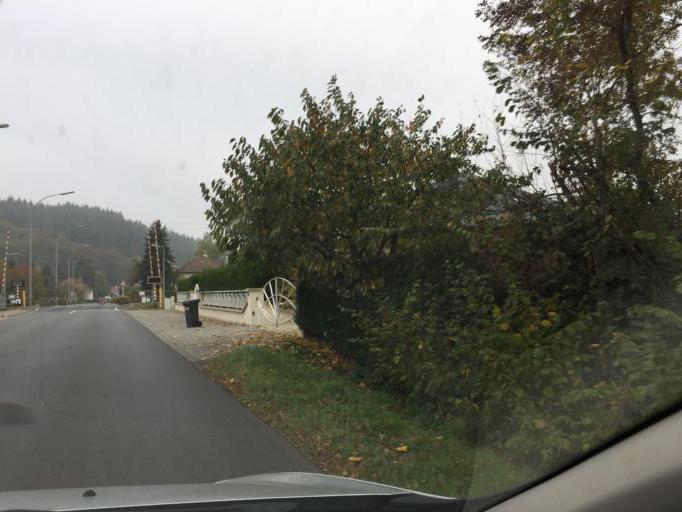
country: LU
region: Luxembourg
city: Moutfort
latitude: 49.5925
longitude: 6.2530
